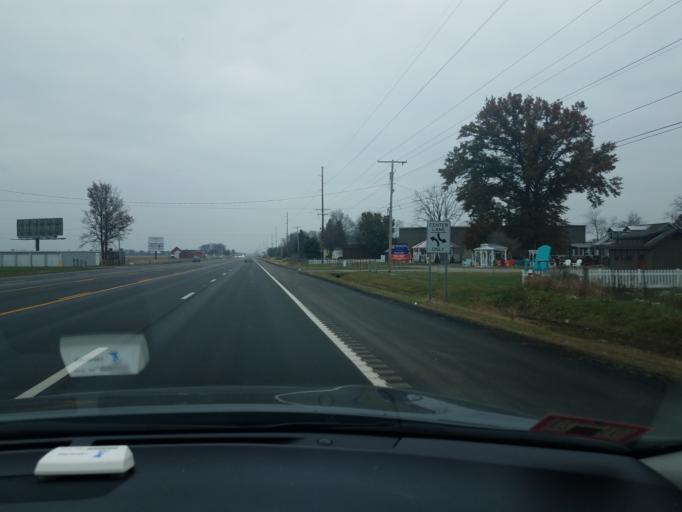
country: US
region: Ohio
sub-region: Erie County
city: Milan
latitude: 41.3771
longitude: -82.6437
